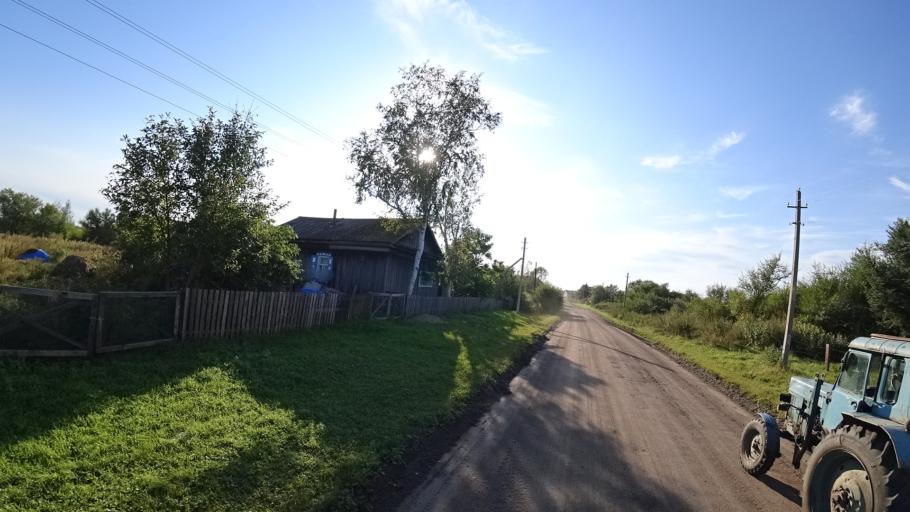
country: RU
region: Amur
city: Arkhara
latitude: 49.3571
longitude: 130.1198
